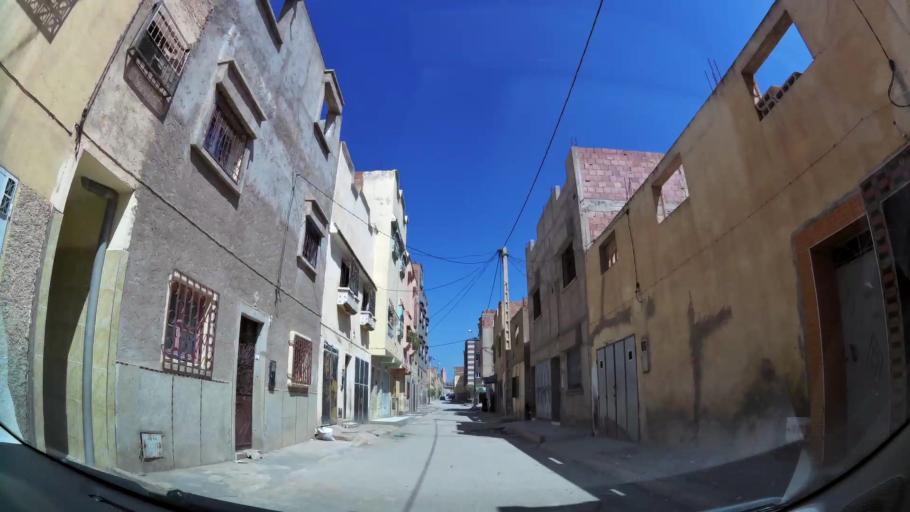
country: MA
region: Oriental
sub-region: Oujda-Angad
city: Oujda
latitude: 34.6675
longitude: -1.9439
